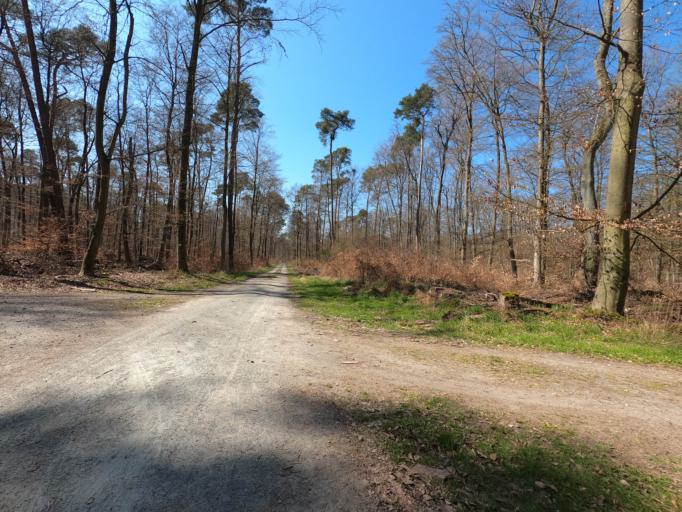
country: DE
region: Hesse
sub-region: Regierungsbezirk Darmstadt
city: Buttelborn
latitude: 49.9395
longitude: 8.5305
